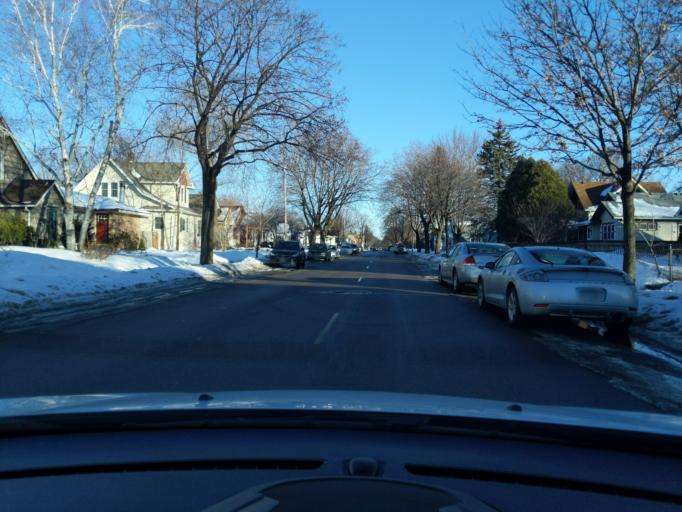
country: US
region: Minnesota
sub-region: Ramsey County
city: Lauderdale
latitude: 44.9309
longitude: -93.2128
